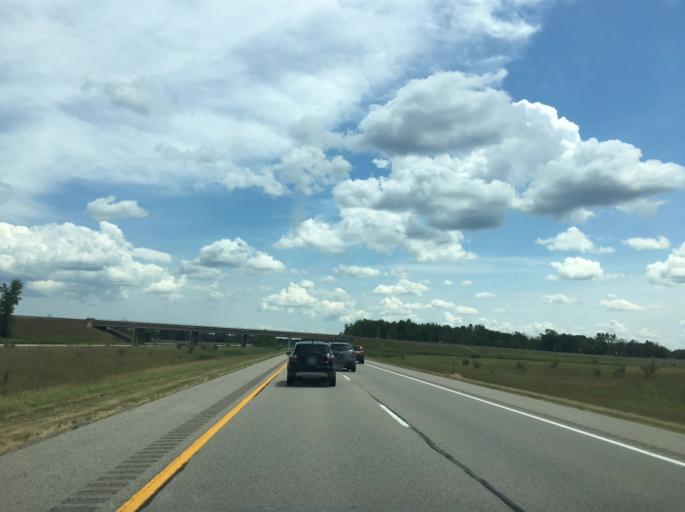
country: US
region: Michigan
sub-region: Ogemaw County
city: Skidway Lake
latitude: 44.1332
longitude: -84.1337
